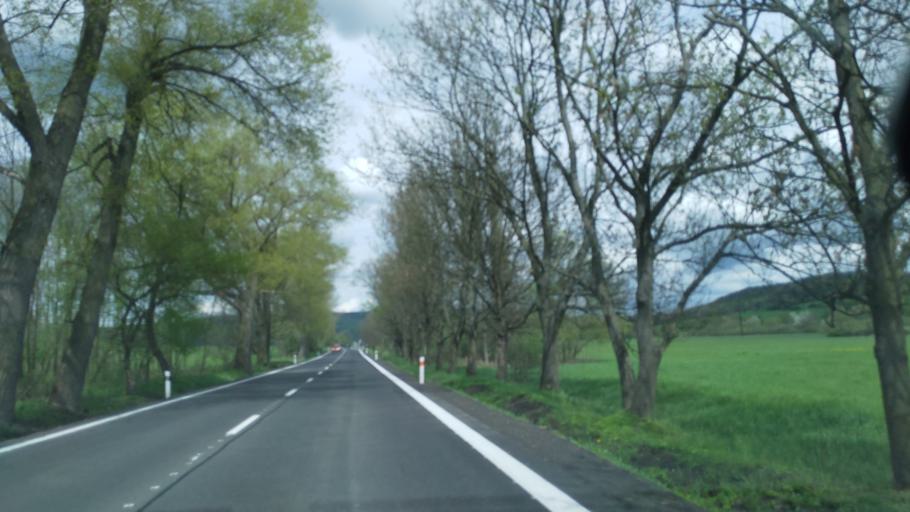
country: CZ
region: Ustecky
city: Libouchec
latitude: 50.7405
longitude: 14.0180
